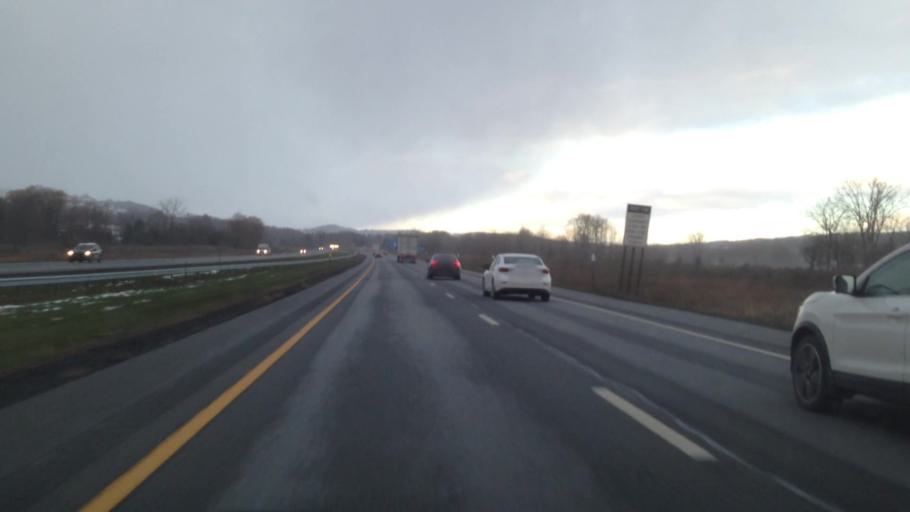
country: US
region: New York
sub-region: Montgomery County
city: Saint Johnsville
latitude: 43.0038
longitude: -74.7670
